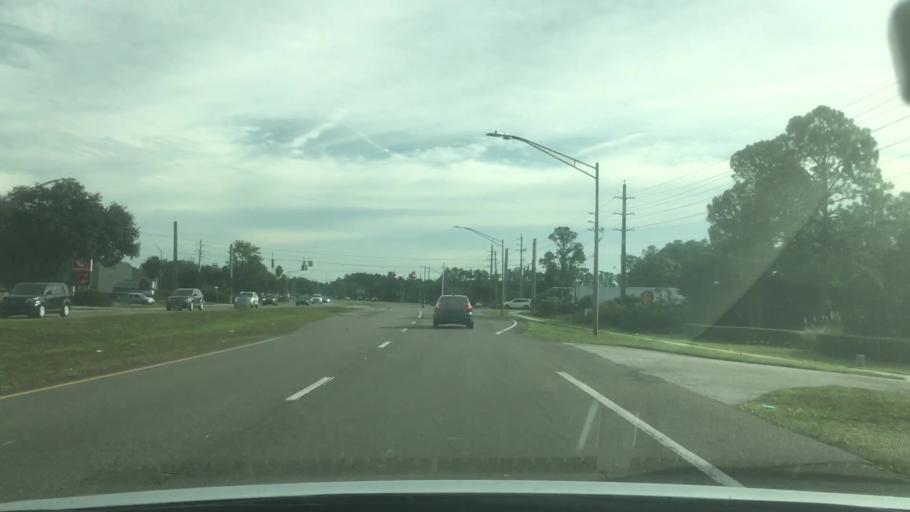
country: US
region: Florida
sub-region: Duval County
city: Neptune Beach
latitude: 30.2825
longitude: -81.5256
